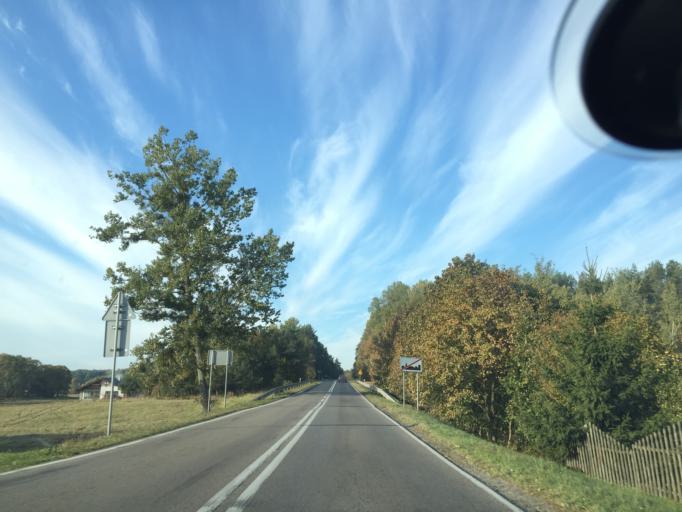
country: PL
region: Warmian-Masurian Voivodeship
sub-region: Powiat lidzbarski
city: Lidzbark Warminski
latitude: 54.1602
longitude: 20.6444
